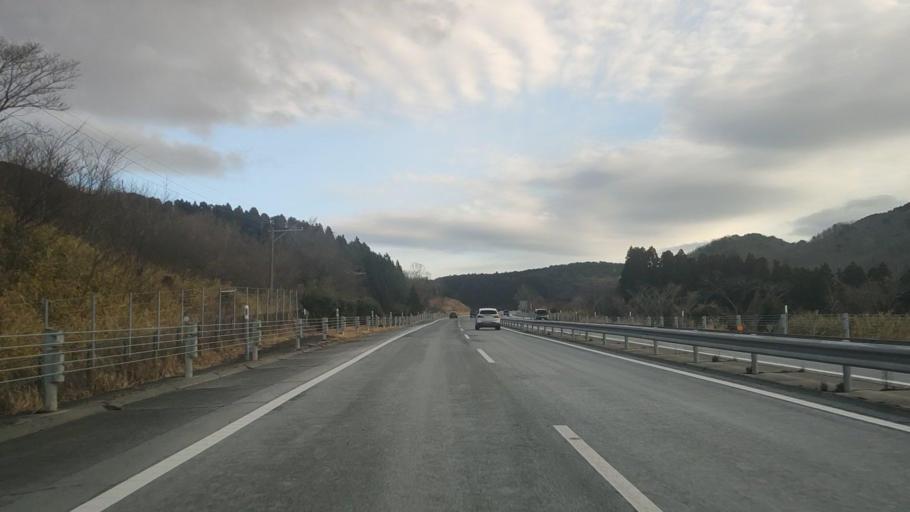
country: JP
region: Oita
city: Beppu
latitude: 33.2884
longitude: 131.3497
